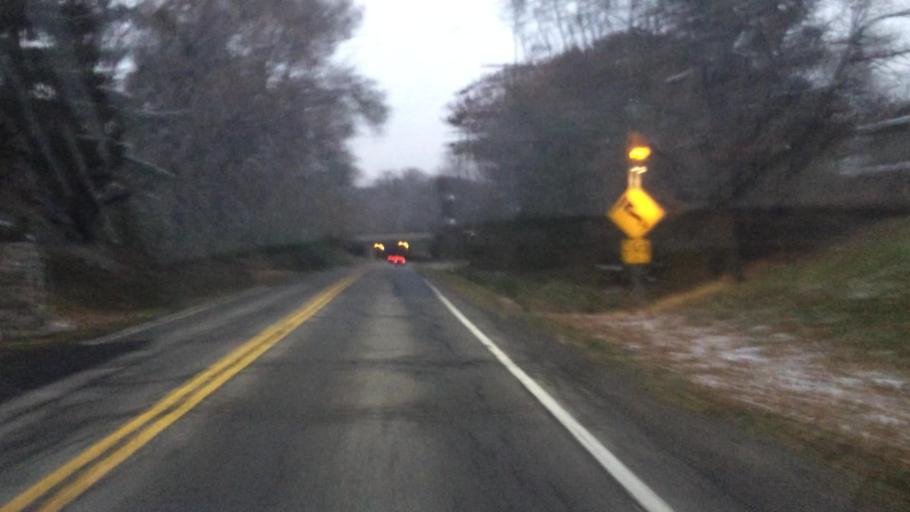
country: US
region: Ohio
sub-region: Cuyahoga County
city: Olmsted Falls
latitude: 41.3550
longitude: -81.8929
